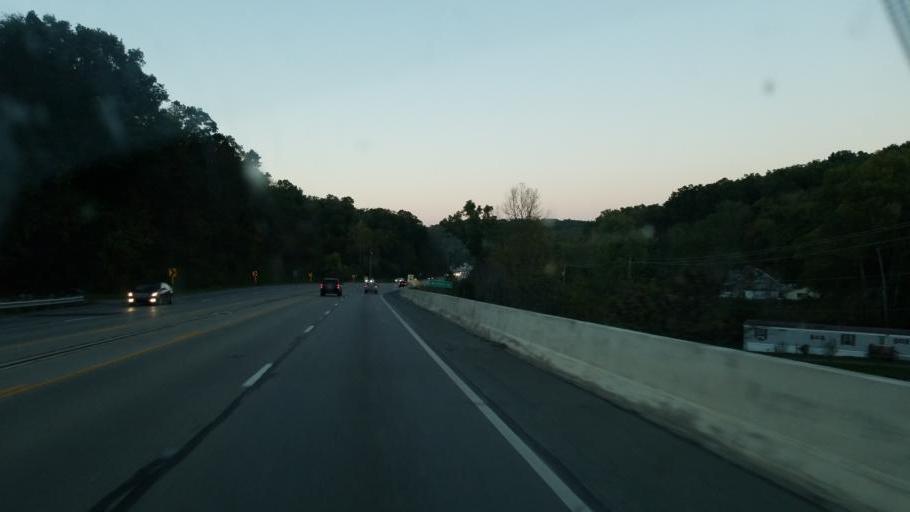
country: US
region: Ohio
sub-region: Pike County
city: Waverly
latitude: 39.2202
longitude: -82.9842
